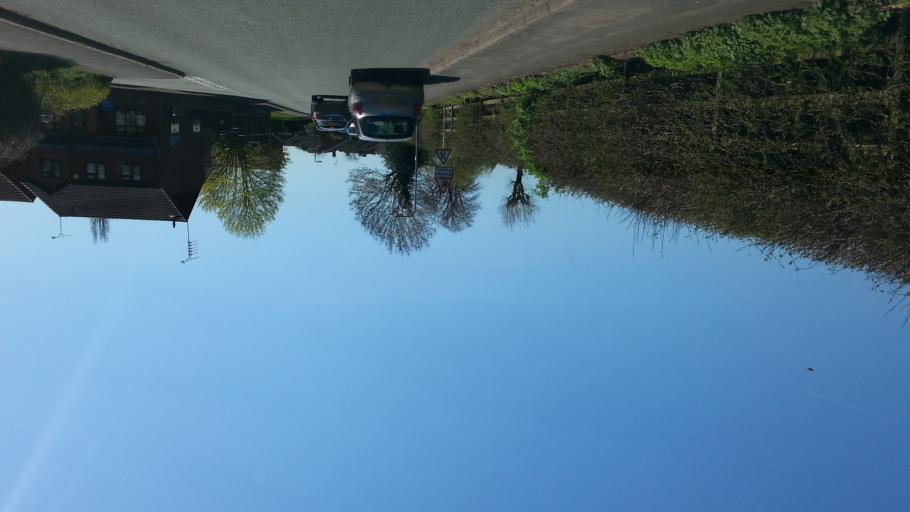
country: GB
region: England
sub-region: Staffordshire
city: Brewood
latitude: 52.6599
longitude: -2.1391
